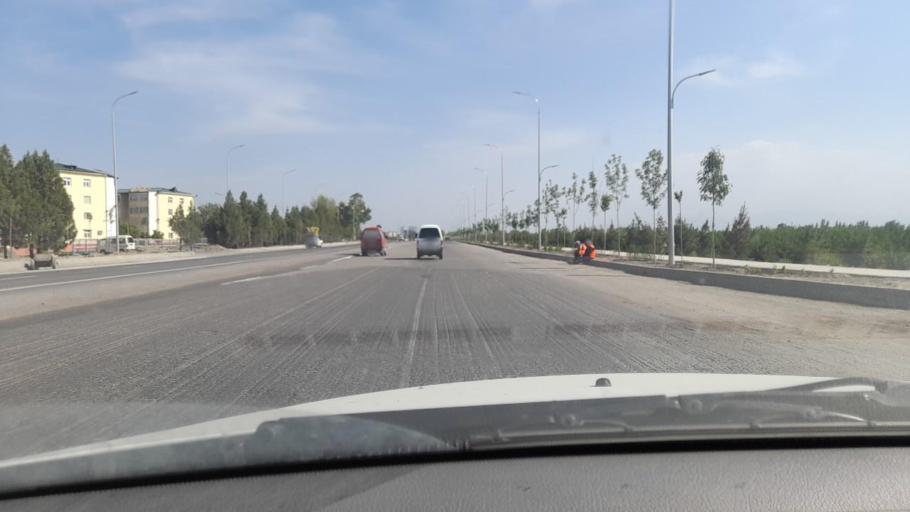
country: UZ
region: Samarqand
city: Daxbet
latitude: 39.7533
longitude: 66.9197
